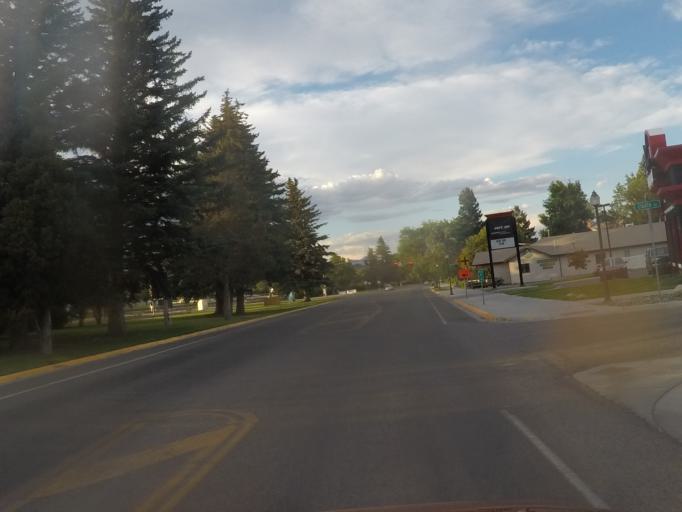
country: US
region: Montana
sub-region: Park County
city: Livingston
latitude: 45.6575
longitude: -110.5687
